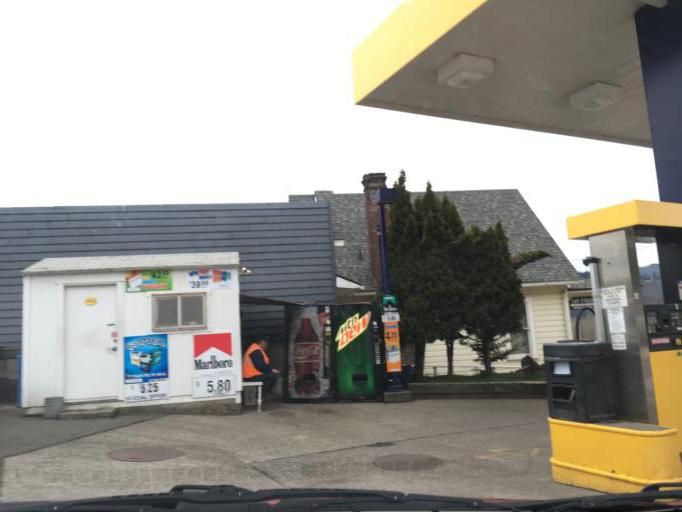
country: US
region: Oregon
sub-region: Hood River County
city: Hood River
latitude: 45.7082
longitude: -121.5112
